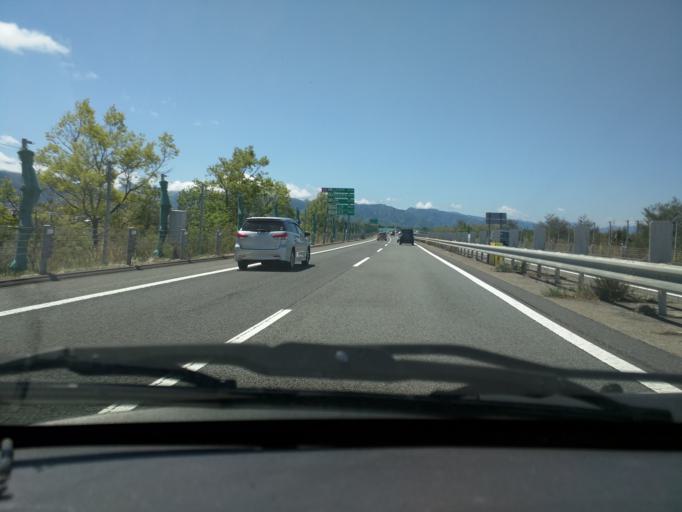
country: JP
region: Nagano
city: Nakano
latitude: 36.7207
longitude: 138.3140
